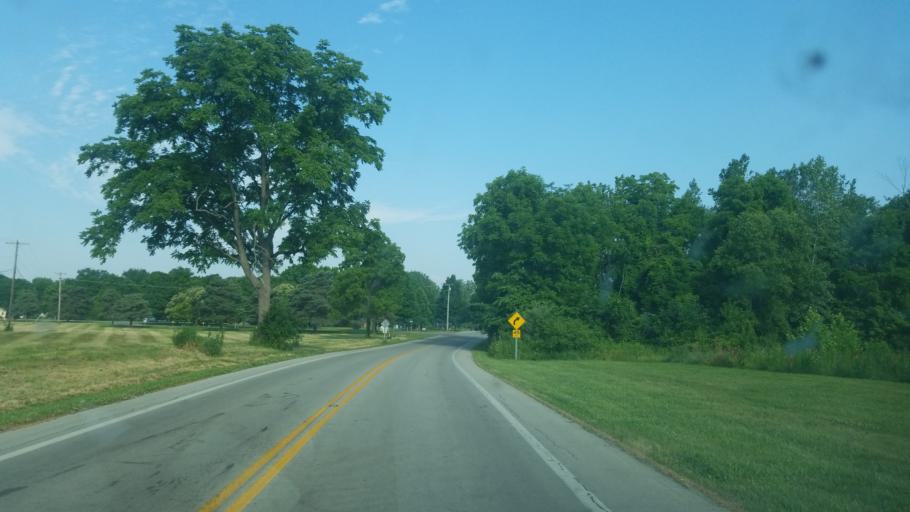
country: US
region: Ohio
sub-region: Logan County
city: Russells Point
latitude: 40.4782
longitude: -83.8574
